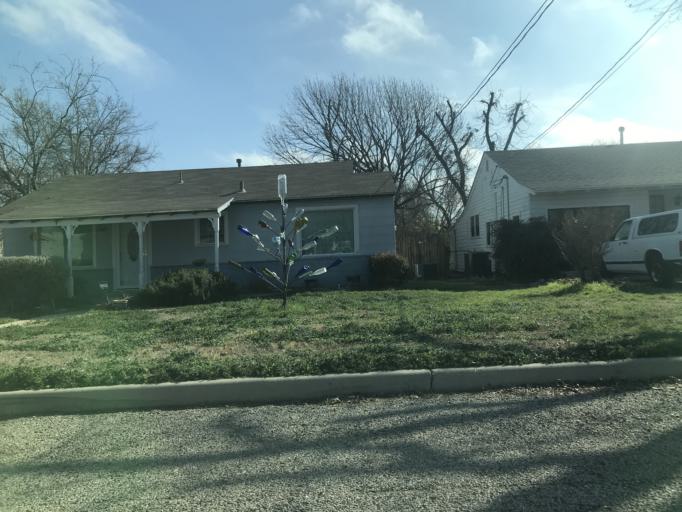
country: US
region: Texas
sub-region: Tom Green County
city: San Angelo
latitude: 31.4459
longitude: -100.4597
